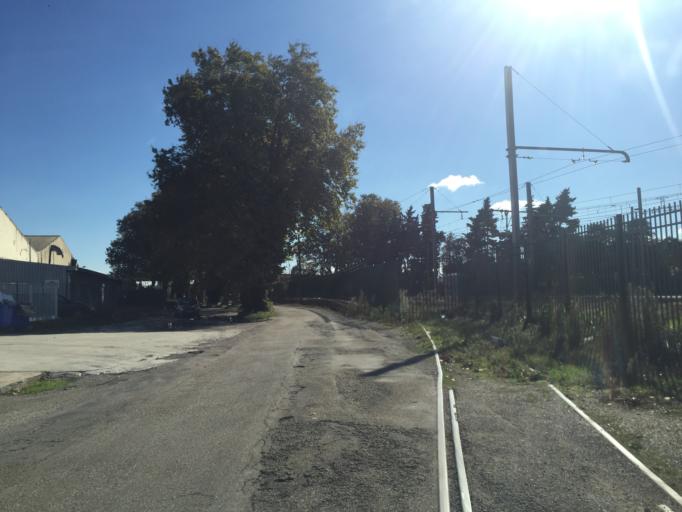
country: FR
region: Provence-Alpes-Cote d'Azur
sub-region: Departement du Vaucluse
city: Montfavet
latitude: 43.9342
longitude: 4.8451
